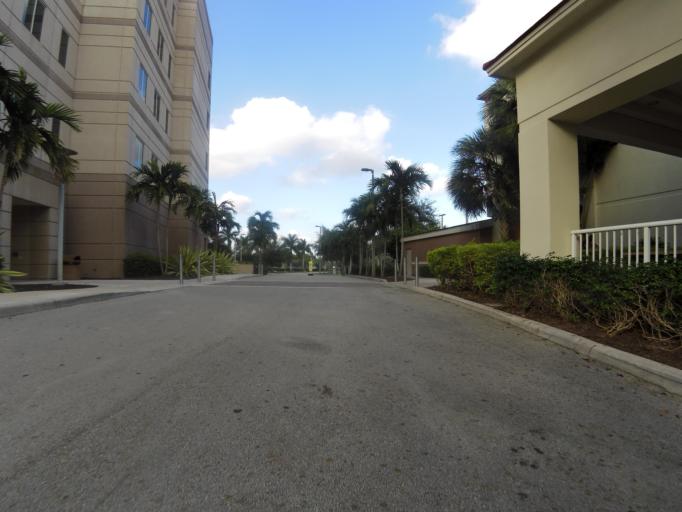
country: US
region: Florida
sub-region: Broward County
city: Davie
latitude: 26.0801
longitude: -80.2417
